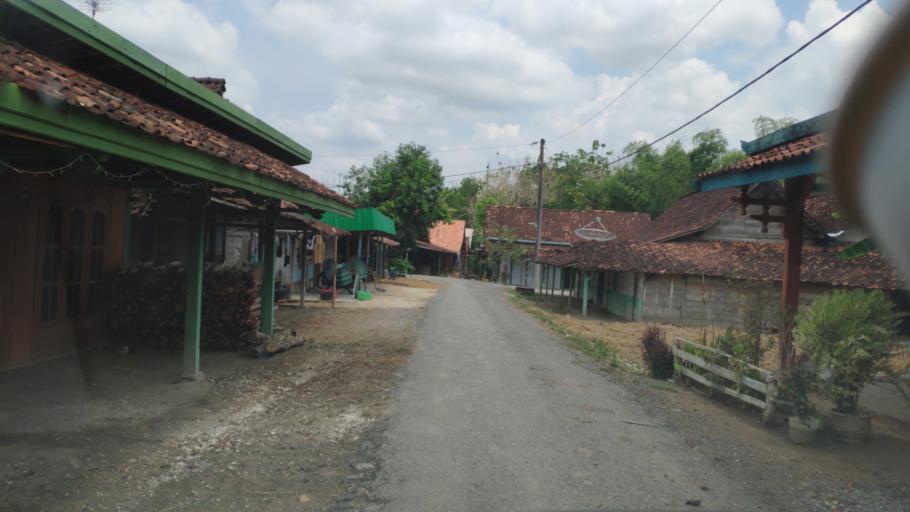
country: ID
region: Central Java
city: Gumiring
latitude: -7.0411
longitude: 111.3904
